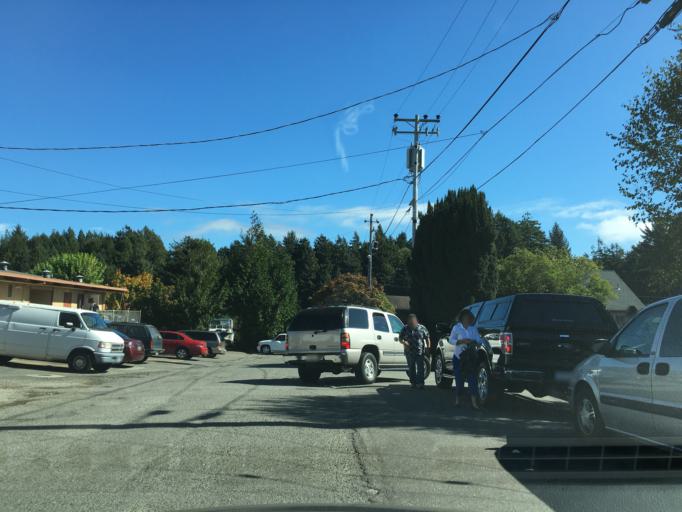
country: US
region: California
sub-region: Humboldt County
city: Myrtletown
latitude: 40.7871
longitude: -124.1393
